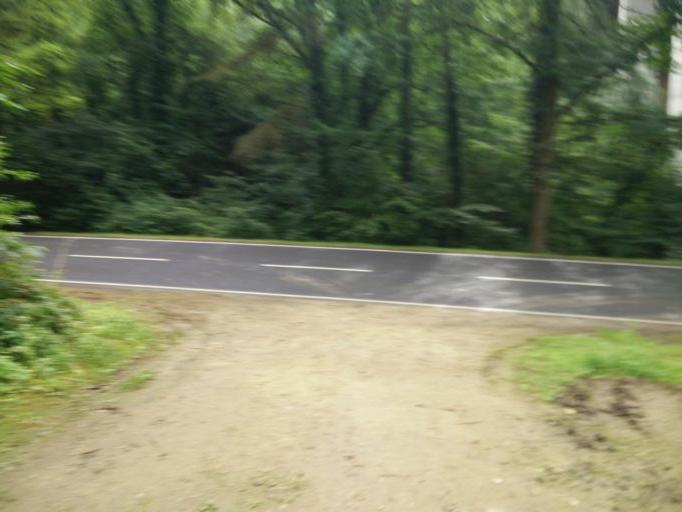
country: LU
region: Luxembourg
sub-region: Canton de Luxembourg
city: Bertrange
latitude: 49.6308
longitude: 6.0469
